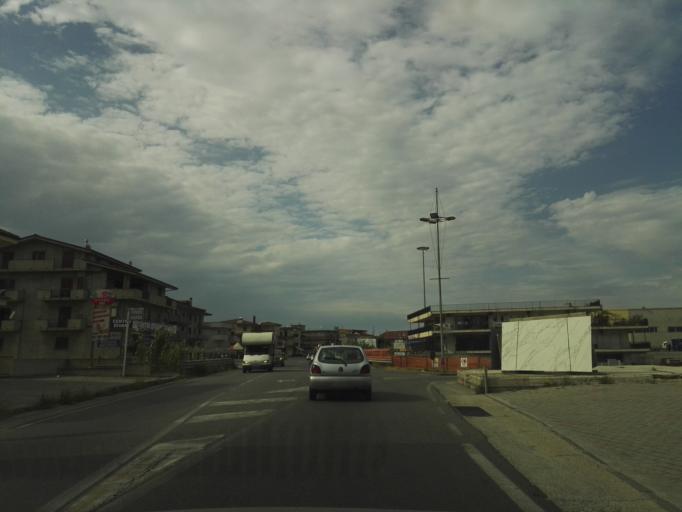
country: IT
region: Calabria
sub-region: Provincia di Catanzaro
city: Marina di Davoli
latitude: 38.6613
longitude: 16.5448
